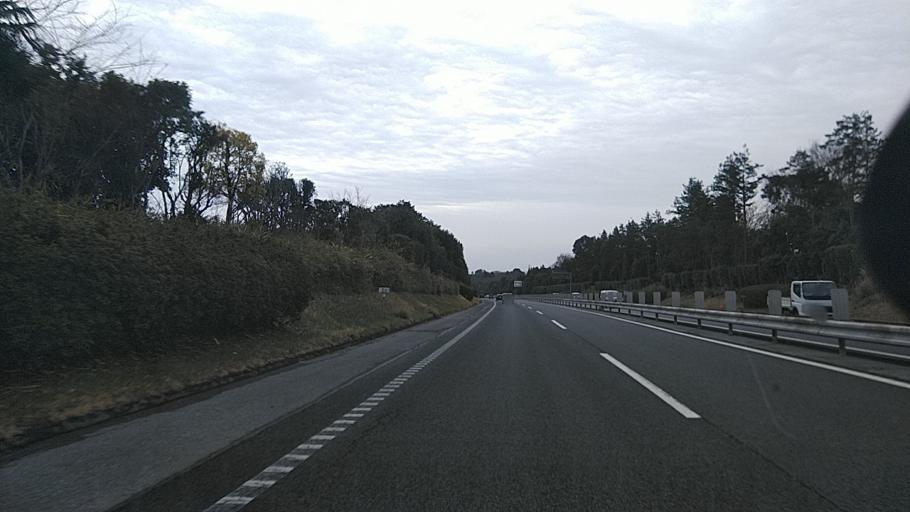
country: JP
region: Chiba
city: Chiba
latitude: 35.5847
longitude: 140.1810
